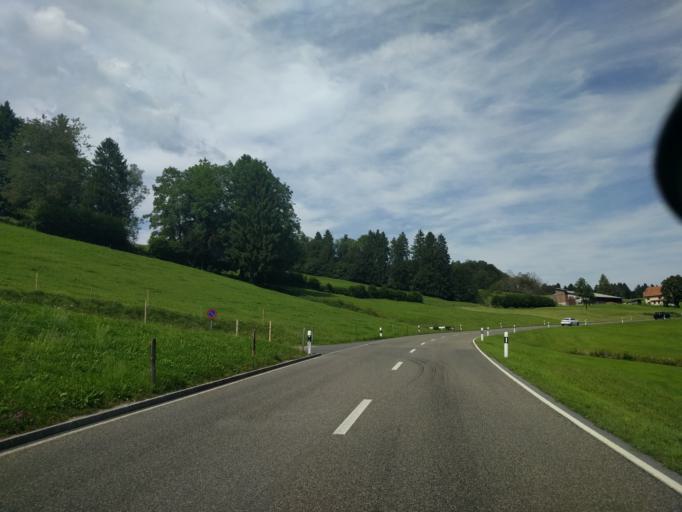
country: CH
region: Saint Gallen
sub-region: Wahlkreis See-Gaster
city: Gommiswald
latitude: 47.2537
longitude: 9.0208
